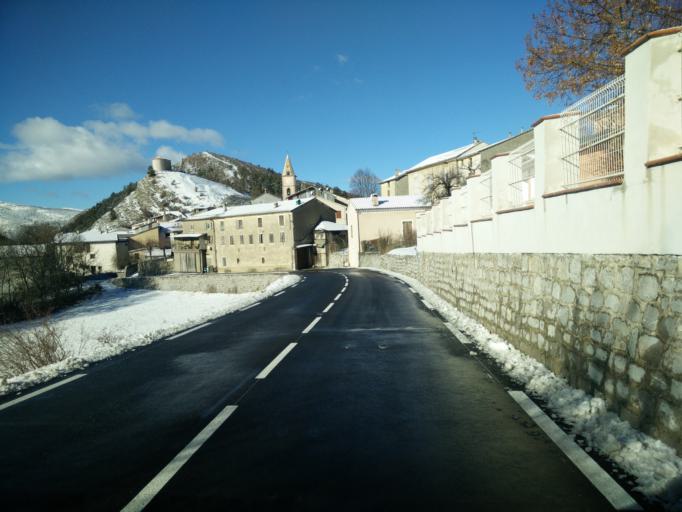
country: FR
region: Provence-Alpes-Cote d'Azur
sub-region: Departement des Alpes-de-Haute-Provence
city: Annot
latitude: 43.9136
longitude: 6.5885
